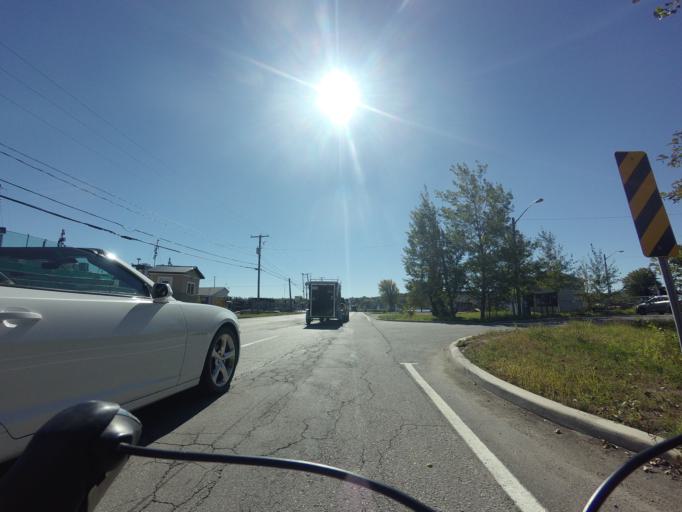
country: CA
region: Ontario
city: Clarence-Rockland
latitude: 45.5276
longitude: -75.4106
